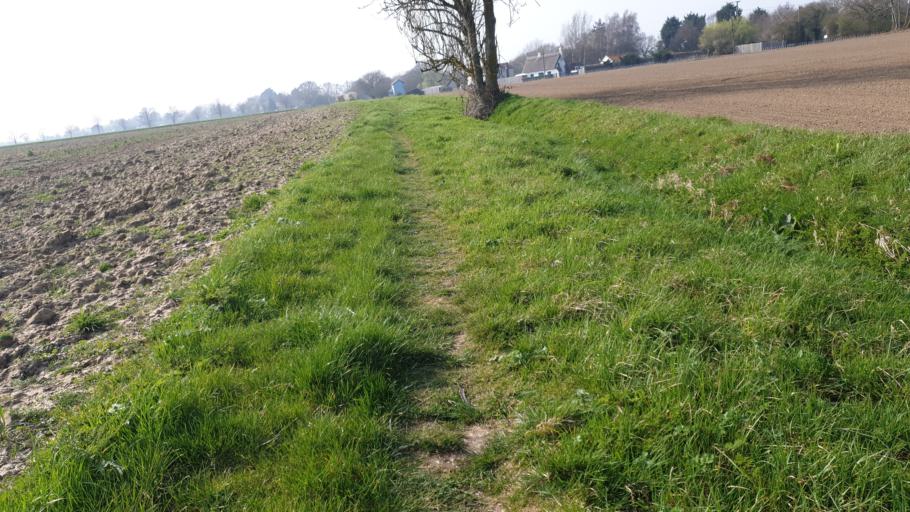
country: GB
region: England
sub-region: Essex
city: Mistley
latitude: 51.9083
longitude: 1.1315
